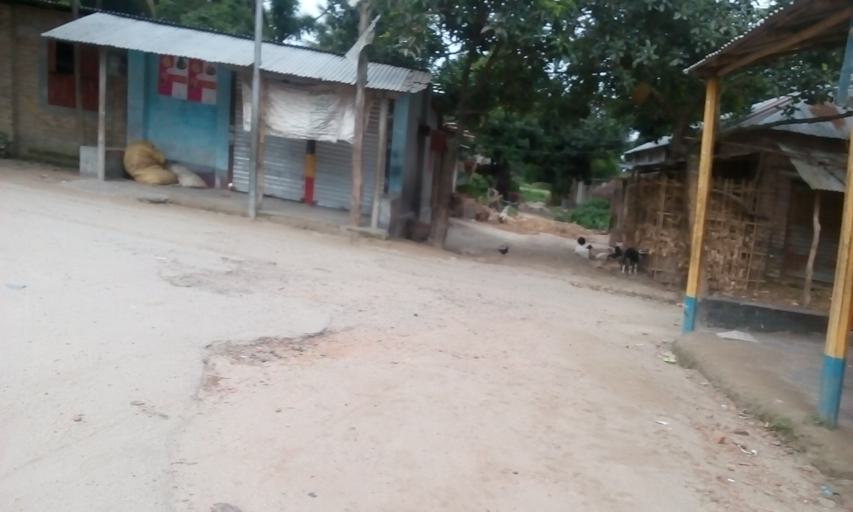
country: IN
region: West Bengal
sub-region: Dakshin Dinajpur
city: Balurghat
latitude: 25.3816
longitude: 88.9833
